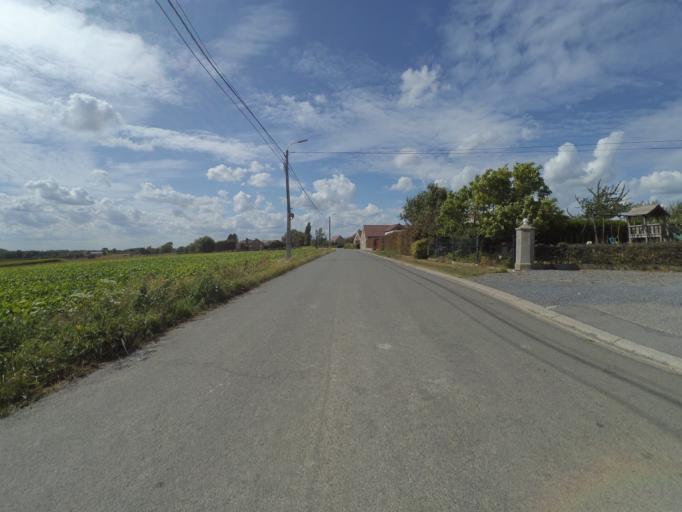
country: BE
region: Flanders
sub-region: Provincie Oost-Vlaanderen
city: Ronse
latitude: 50.7258
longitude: 3.6076
